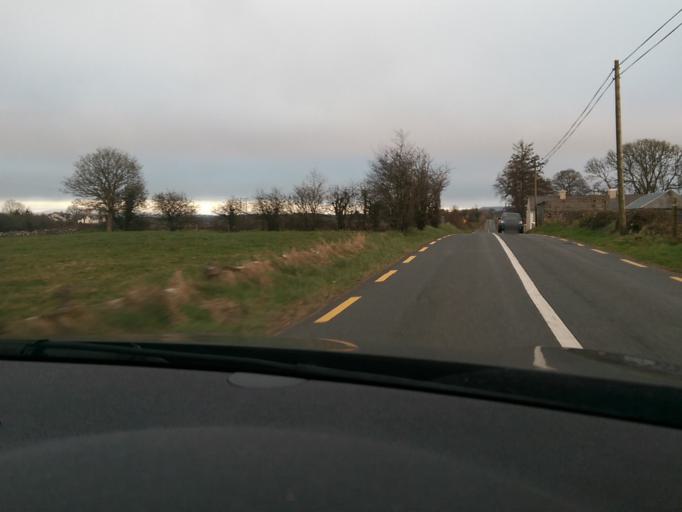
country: IE
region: Connaught
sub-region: Sligo
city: Ballymote
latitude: 54.0156
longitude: -8.5563
